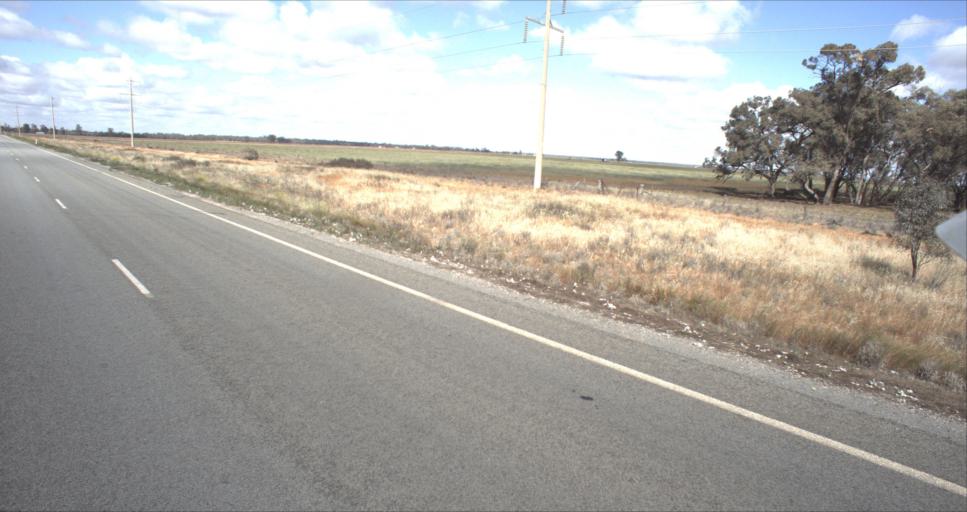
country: AU
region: New South Wales
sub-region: Murrumbidgee Shire
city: Darlington Point
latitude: -34.5767
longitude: 146.1660
